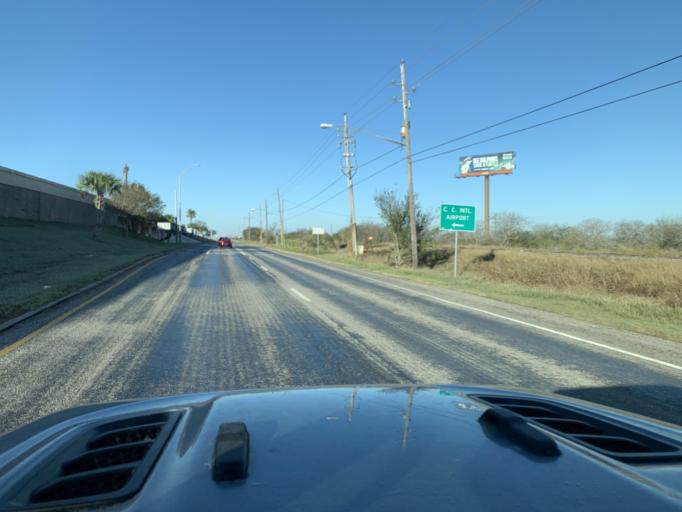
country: US
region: Texas
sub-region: Nueces County
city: Corpus Christi
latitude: 27.7852
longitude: -97.5011
